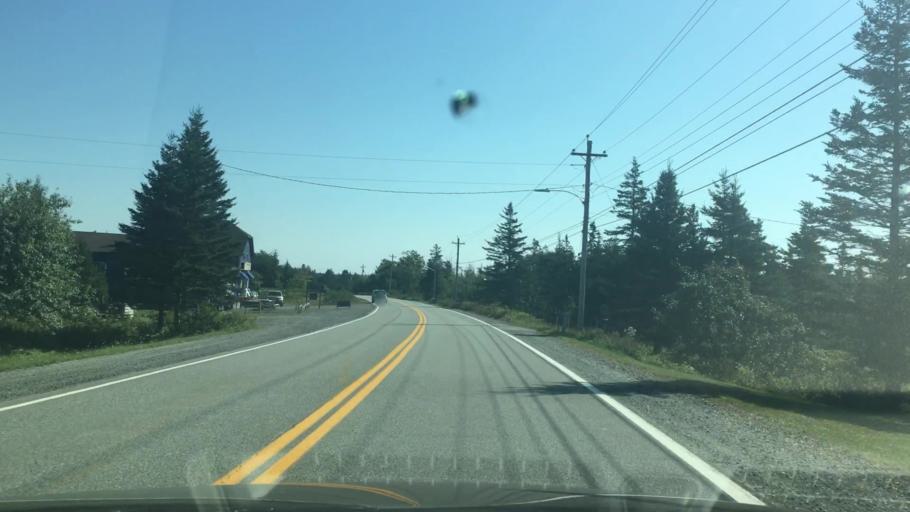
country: CA
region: Nova Scotia
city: Cole Harbour
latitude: 44.7788
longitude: -62.7785
